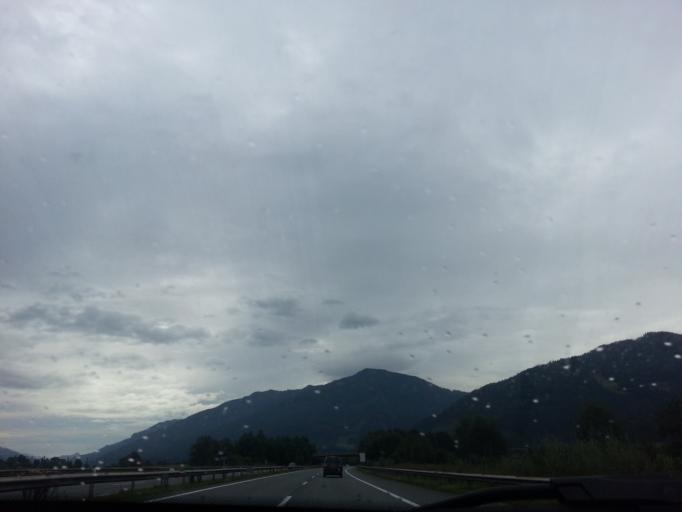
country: AT
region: Styria
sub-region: Politischer Bezirk Liezen
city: Trieben
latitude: 47.5043
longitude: 14.4565
